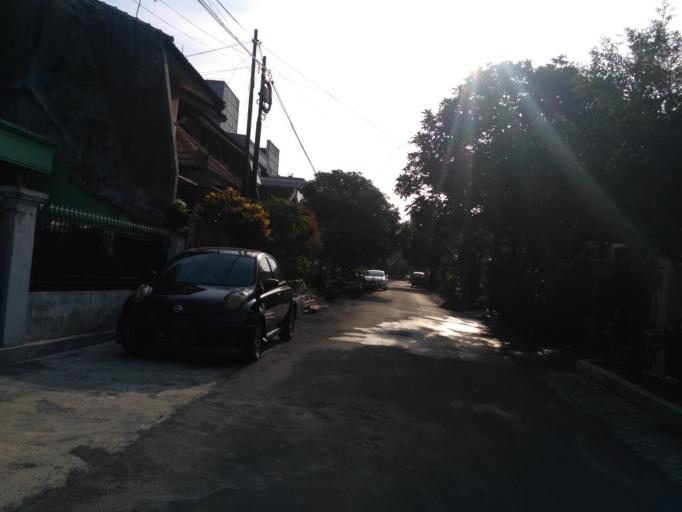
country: ID
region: East Java
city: Malang
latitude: -7.9393
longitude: 112.6274
